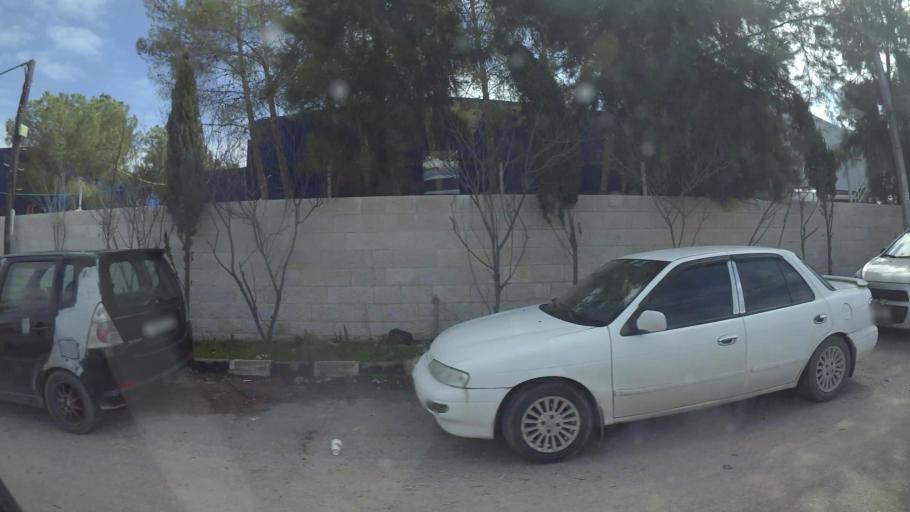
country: JO
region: Amman
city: Al Jubayhah
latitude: 32.0606
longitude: 35.8226
